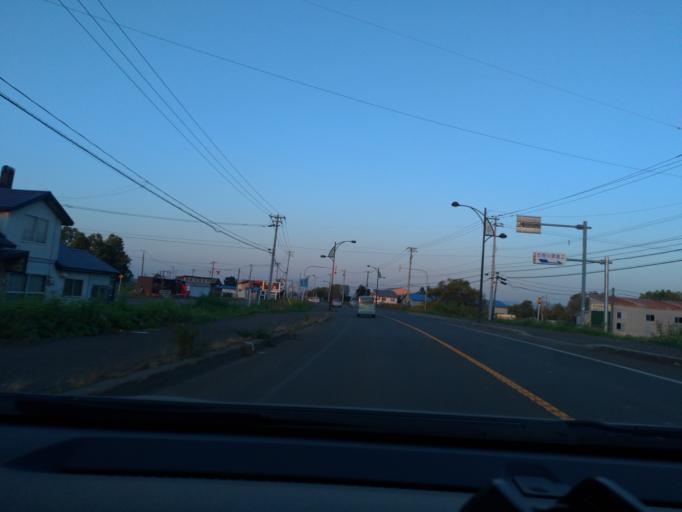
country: JP
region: Hokkaido
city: Iwamizawa
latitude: 43.3296
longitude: 141.6605
